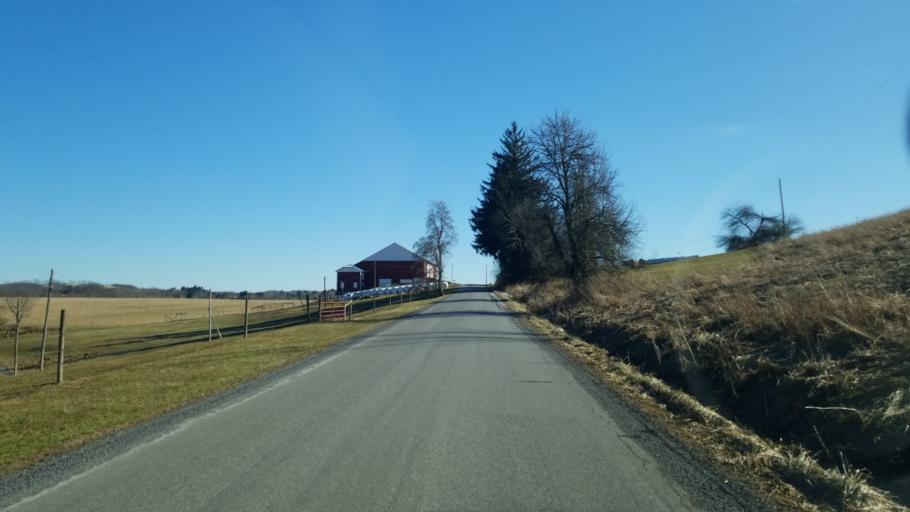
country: US
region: Pennsylvania
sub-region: Jefferson County
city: Sykesville
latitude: 41.0437
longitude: -78.7850
